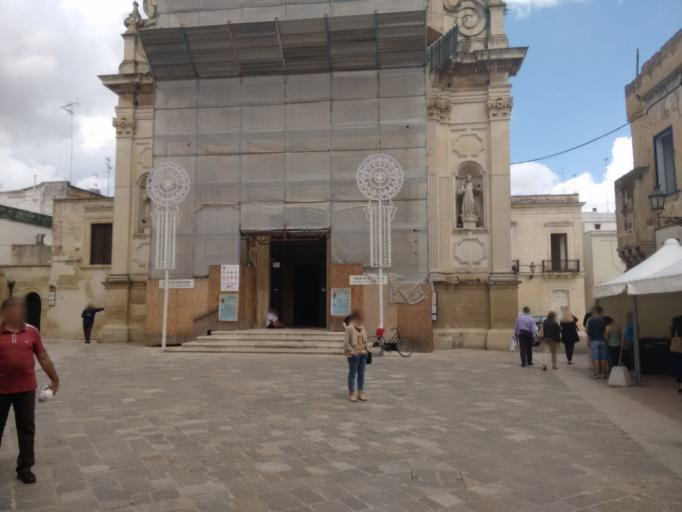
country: IT
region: Apulia
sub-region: Provincia di Lecce
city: Lecce
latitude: 40.3563
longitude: 18.1701
